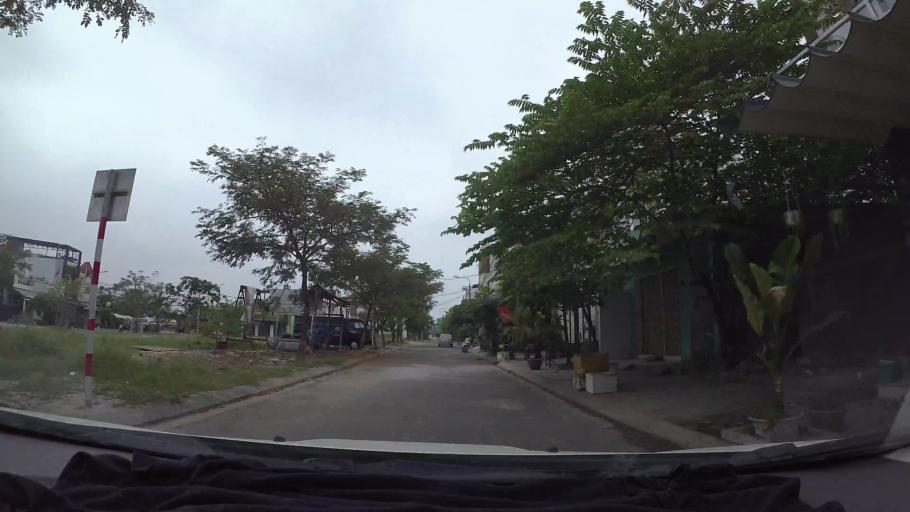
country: VN
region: Da Nang
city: Lien Chieu
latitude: 16.0647
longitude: 108.1702
